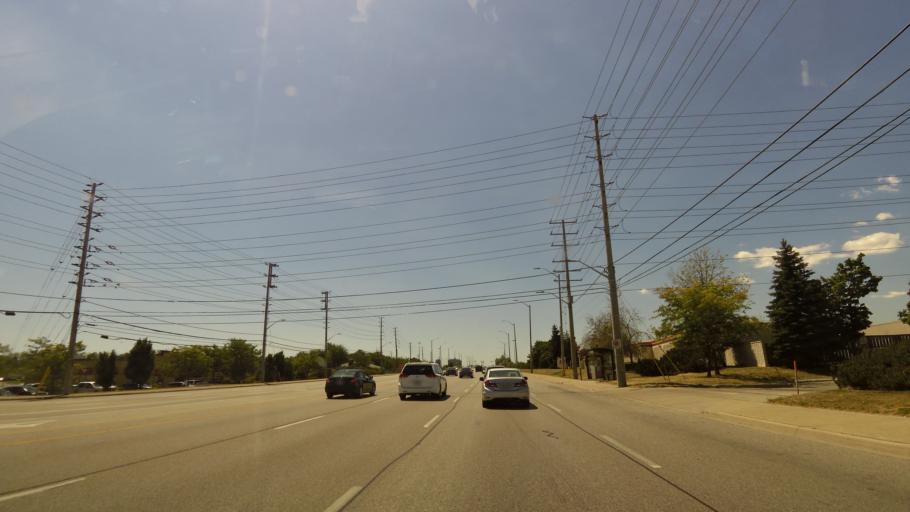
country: CA
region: Ontario
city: Mississauga
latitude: 43.6265
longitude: -79.6311
